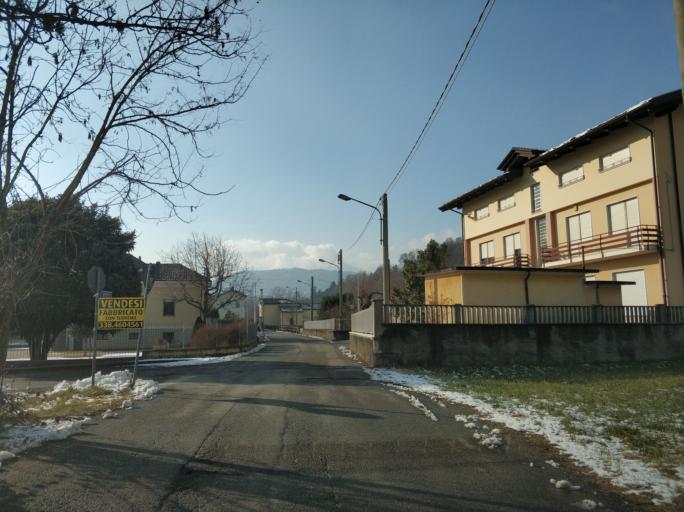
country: IT
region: Piedmont
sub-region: Provincia di Torino
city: Lanzo Torinese
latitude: 45.2745
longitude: 7.4977
